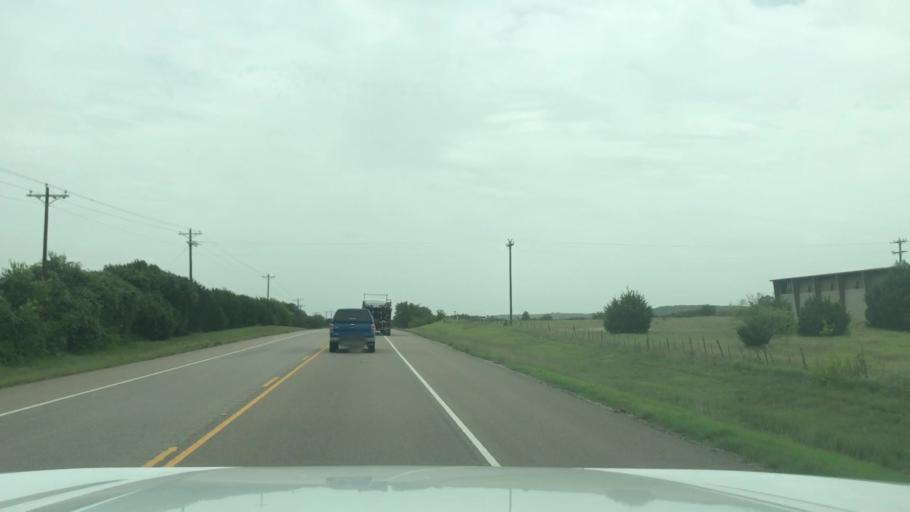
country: US
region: Texas
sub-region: Bosque County
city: Meridian
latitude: 31.9340
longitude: -97.6991
